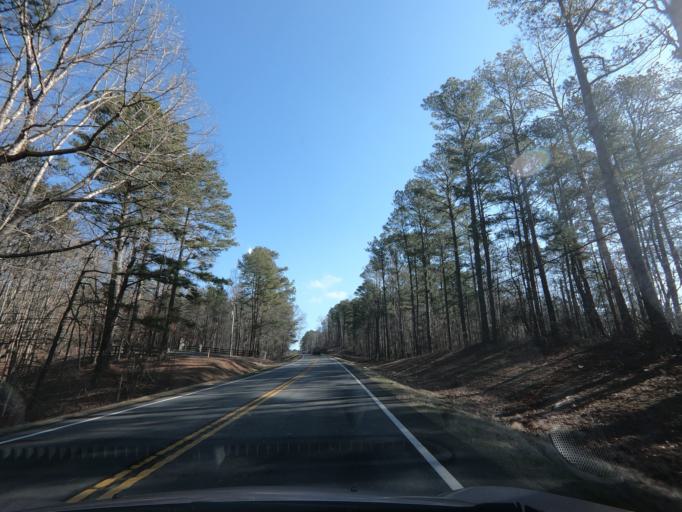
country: US
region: Georgia
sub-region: Cherokee County
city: Ball Ground
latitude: 34.2963
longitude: -84.2551
